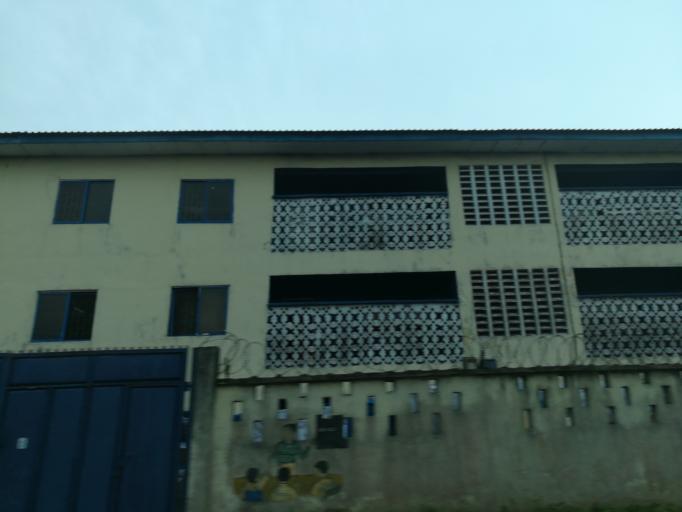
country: NG
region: Rivers
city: Port Harcourt
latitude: 4.8229
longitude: 7.0279
